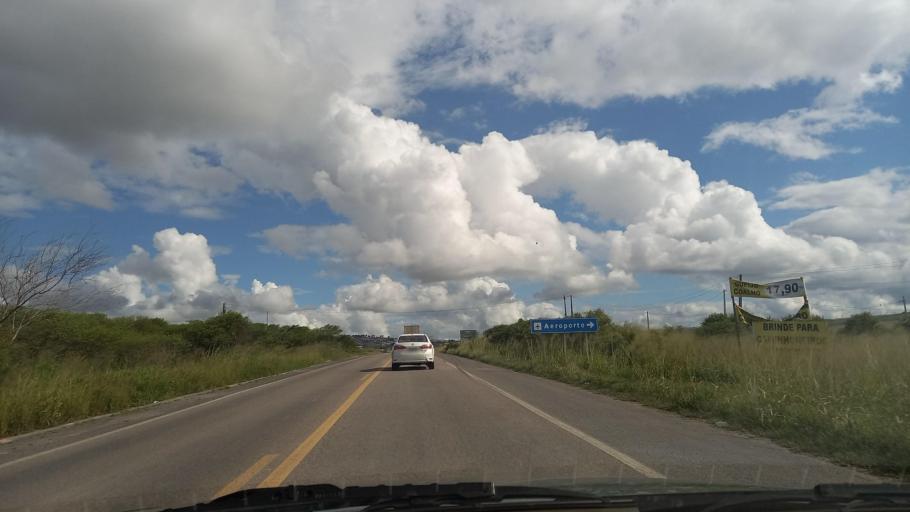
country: BR
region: Pernambuco
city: Garanhuns
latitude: -8.8397
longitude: -36.4569
